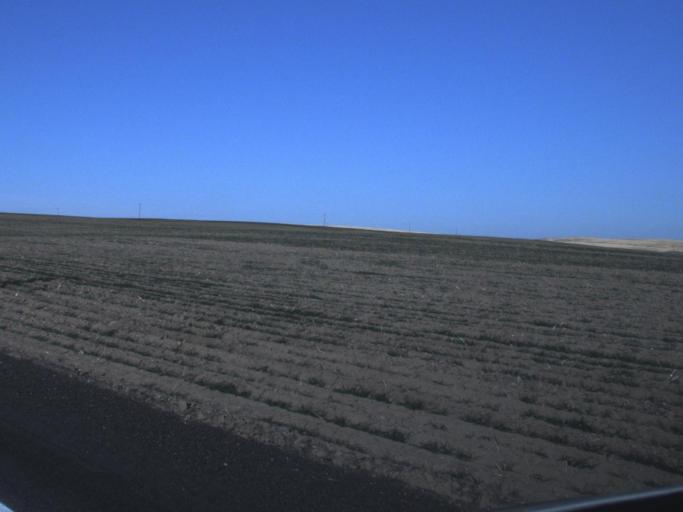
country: US
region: Washington
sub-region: Adams County
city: Ritzville
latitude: 47.0243
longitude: -118.3496
